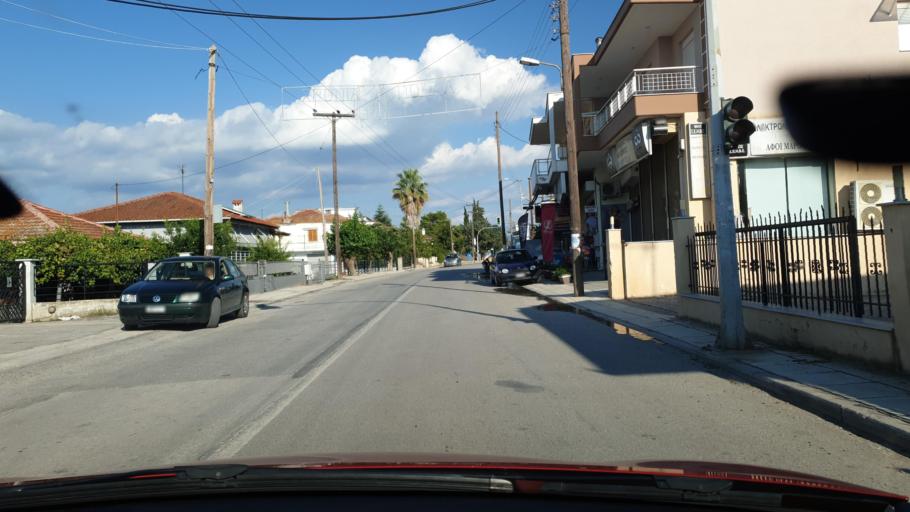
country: GR
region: Central Macedonia
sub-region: Nomos Thessalonikis
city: Agia Paraskevi
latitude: 40.4836
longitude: 23.0494
